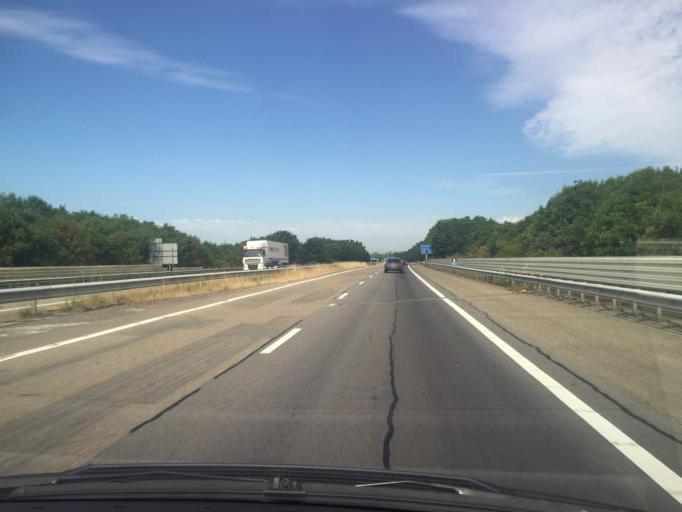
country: NL
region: North Brabant
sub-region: Gemeente Boxmeer
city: Boxmeer
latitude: 51.6638
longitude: 5.9226
